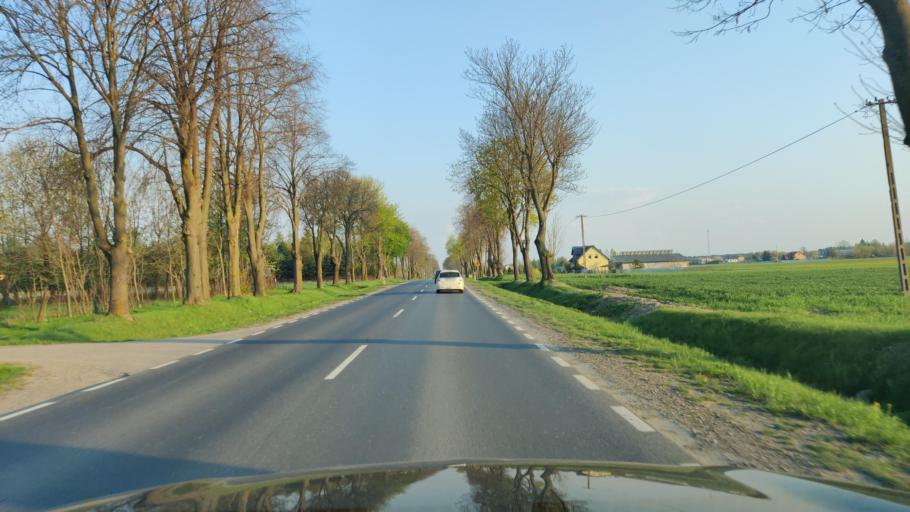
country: PL
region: Masovian Voivodeship
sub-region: Powiat pultuski
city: Pultusk
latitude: 52.6274
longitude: 21.0988
